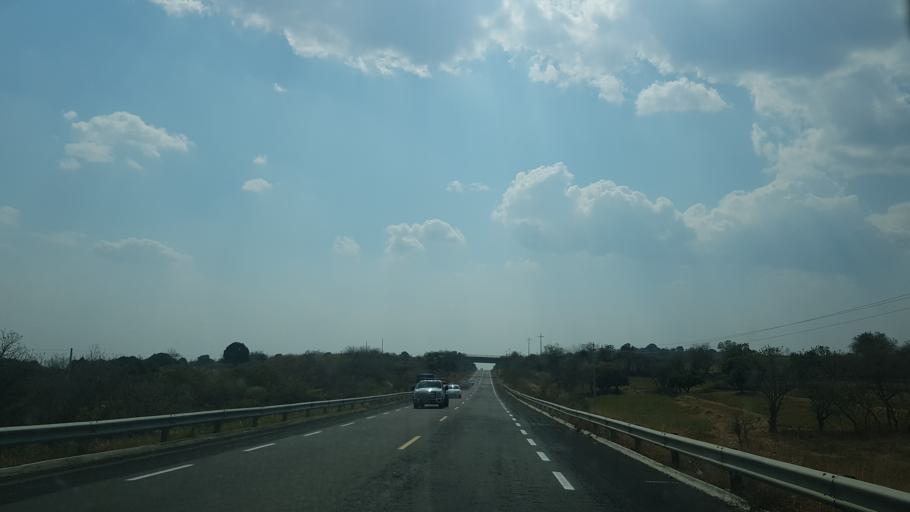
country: MX
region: Puebla
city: San Juan Amecac
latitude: 18.8166
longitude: -98.6603
